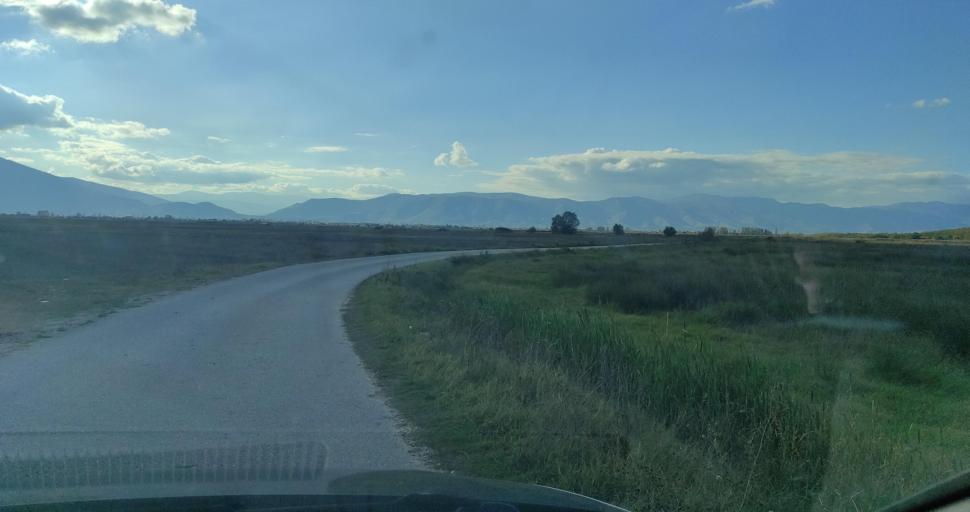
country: MK
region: Prilep
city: Topolcani
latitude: 41.2781
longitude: 21.4302
